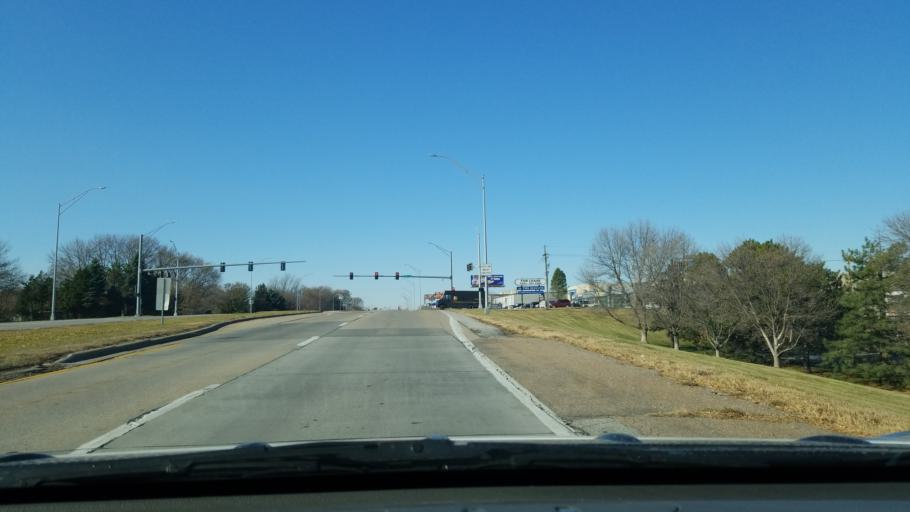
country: US
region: Nebraska
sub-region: Douglas County
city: Ralston
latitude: 41.2126
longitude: -96.0706
